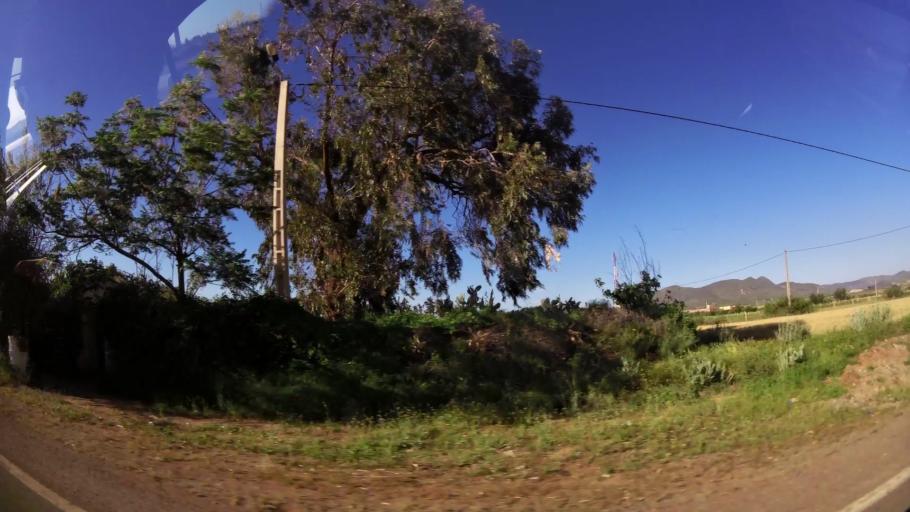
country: MA
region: Oriental
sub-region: Berkane-Taourirt
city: Ahfir
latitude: 34.9869
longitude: -2.1493
